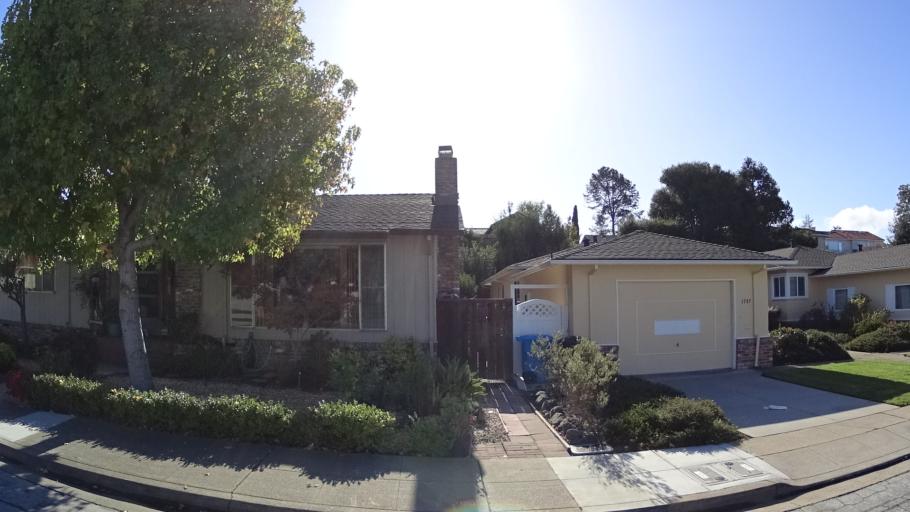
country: US
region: California
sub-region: San Mateo County
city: Millbrae
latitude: 37.5902
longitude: -122.3867
